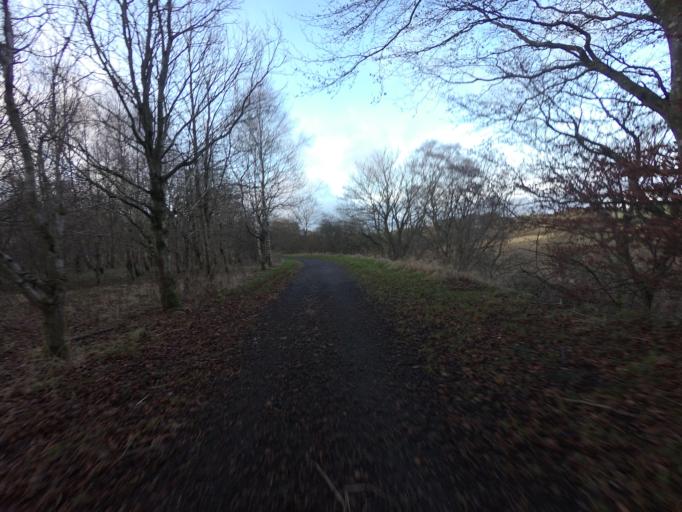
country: GB
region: Scotland
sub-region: West Lothian
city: West Calder
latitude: 55.8776
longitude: -3.5718
